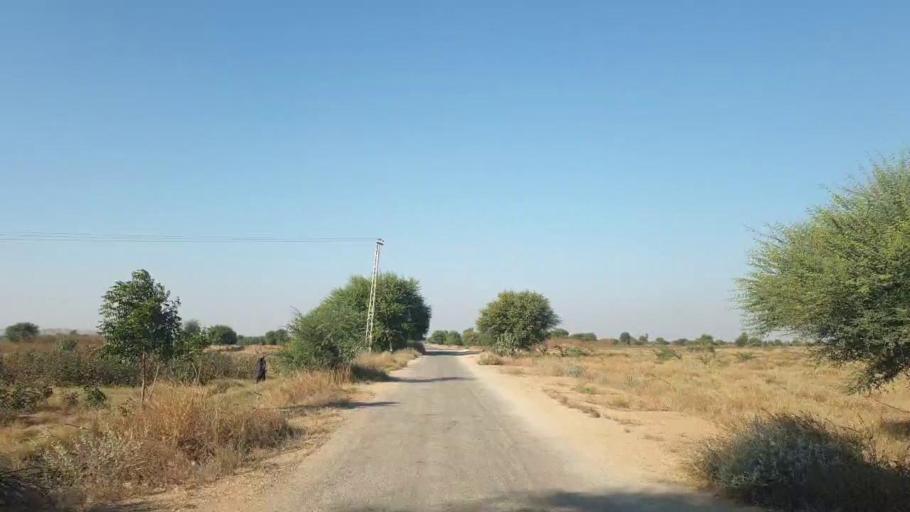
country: PK
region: Sindh
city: Malir Cantonment
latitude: 25.4217
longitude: 67.4621
